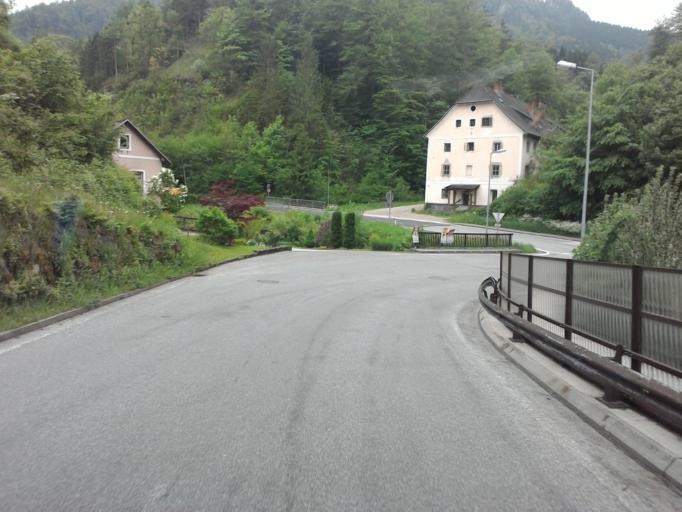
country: AT
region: Styria
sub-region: Politischer Bezirk Liezen
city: Landl
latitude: 47.6654
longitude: 14.7116
